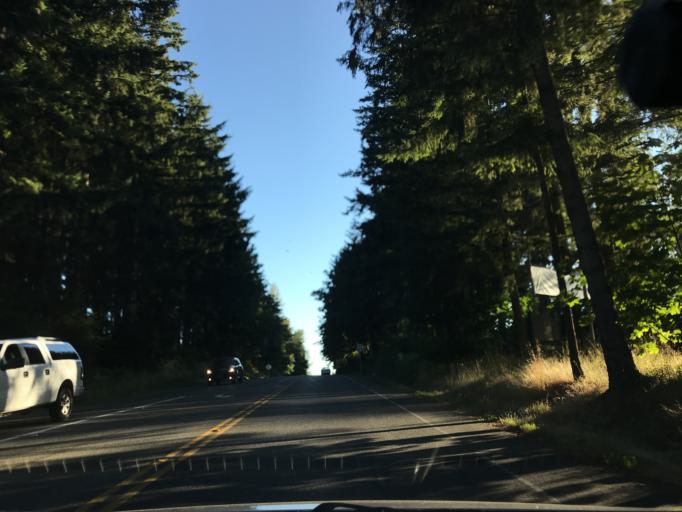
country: US
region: Washington
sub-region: Pierce County
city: Sumner
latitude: 47.2220
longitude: -122.2060
